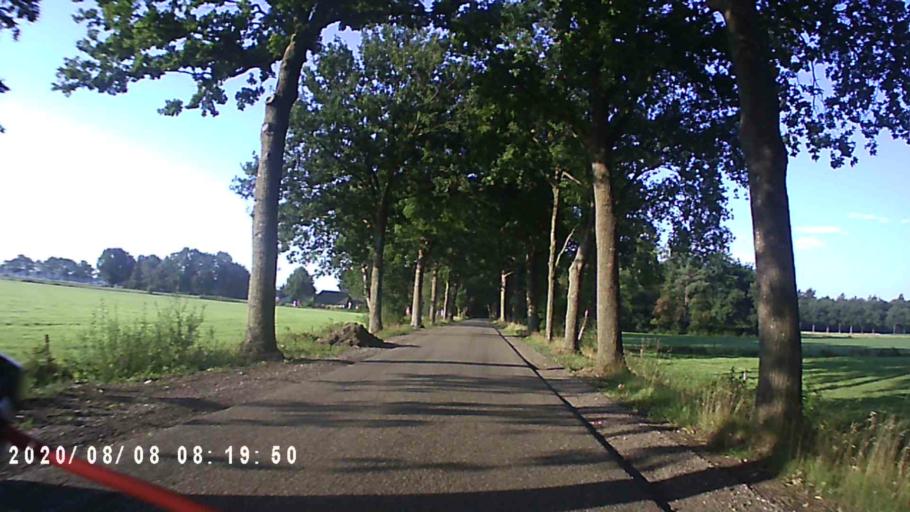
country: NL
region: Groningen
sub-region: Gemeente Leek
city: Leek
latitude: 53.0955
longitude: 6.3152
